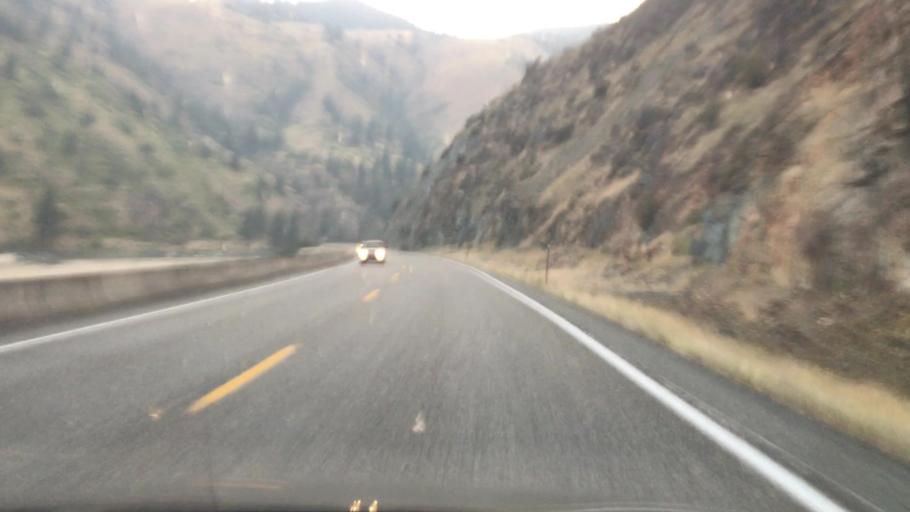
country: US
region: Idaho
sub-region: Idaho County
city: Grangeville
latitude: 45.6213
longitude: -116.2937
